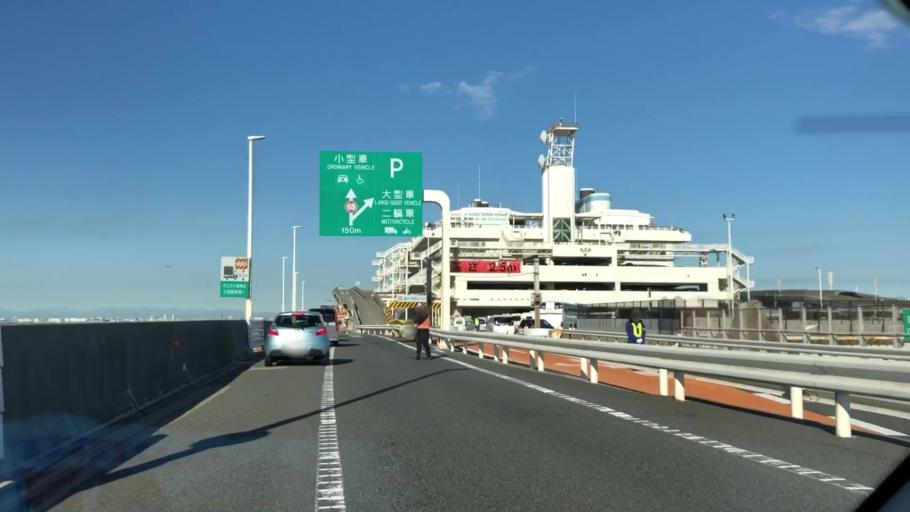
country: JP
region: Chiba
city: Kisarazu
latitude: 35.4627
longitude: 139.8761
